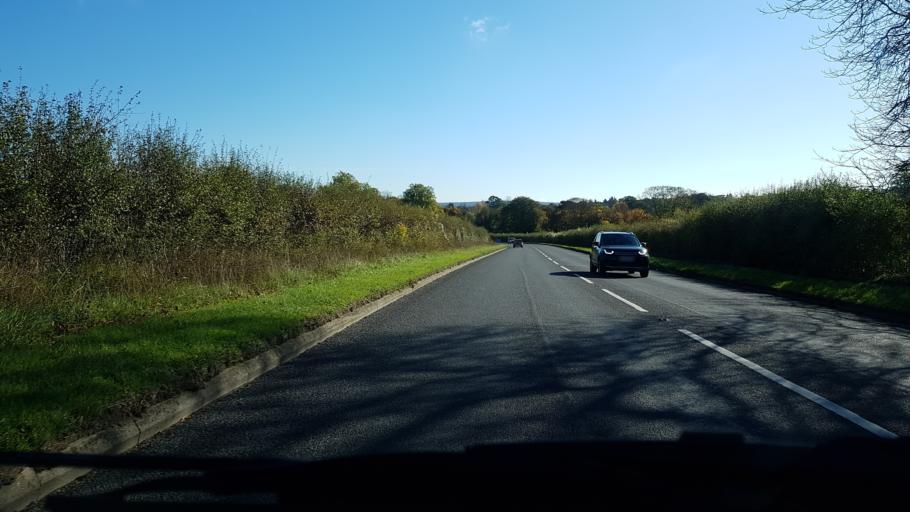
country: GB
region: England
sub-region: Surrey
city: East Horsley
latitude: 51.2228
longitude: -0.4629
